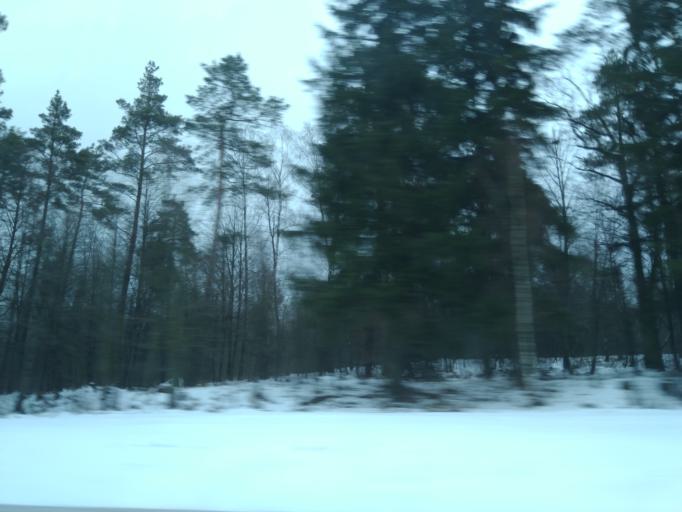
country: BY
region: Minsk
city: Nyasvizh
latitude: 53.2511
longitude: 26.6205
